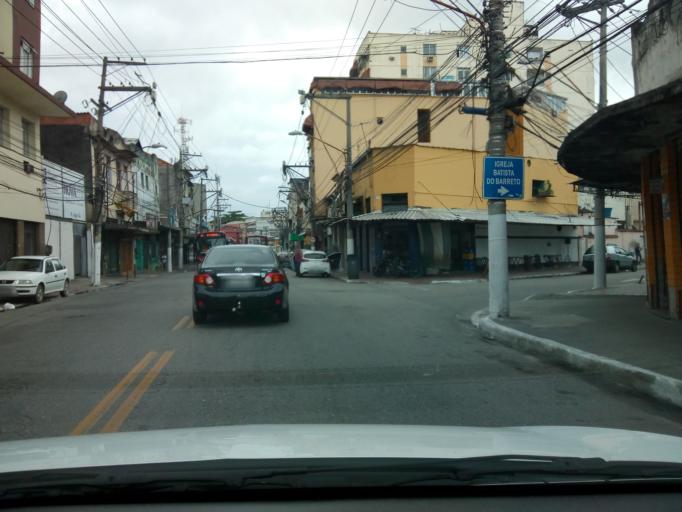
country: BR
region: Rio de Janeiro
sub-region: Niteroi
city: Niteroi
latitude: -22.8612
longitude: -43.1027
